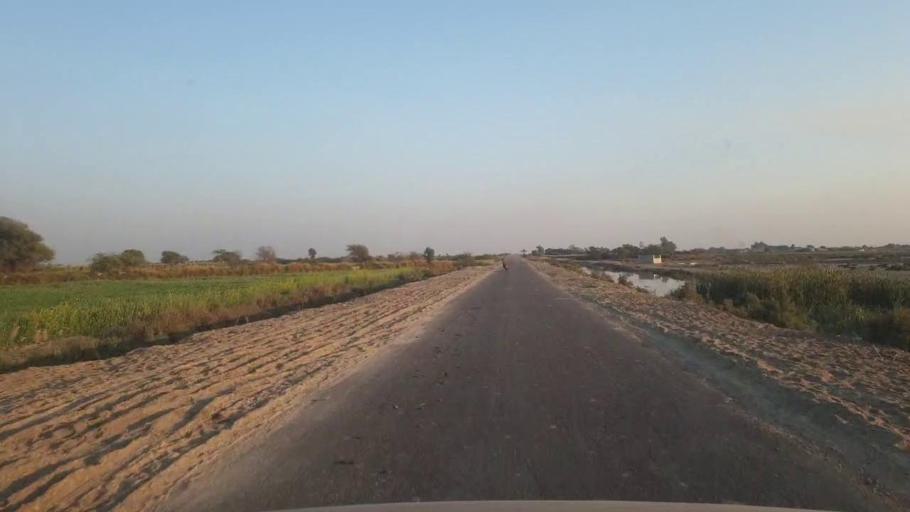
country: PK
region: Sindh
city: Chambar
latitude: 25.2838
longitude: 68.9106
